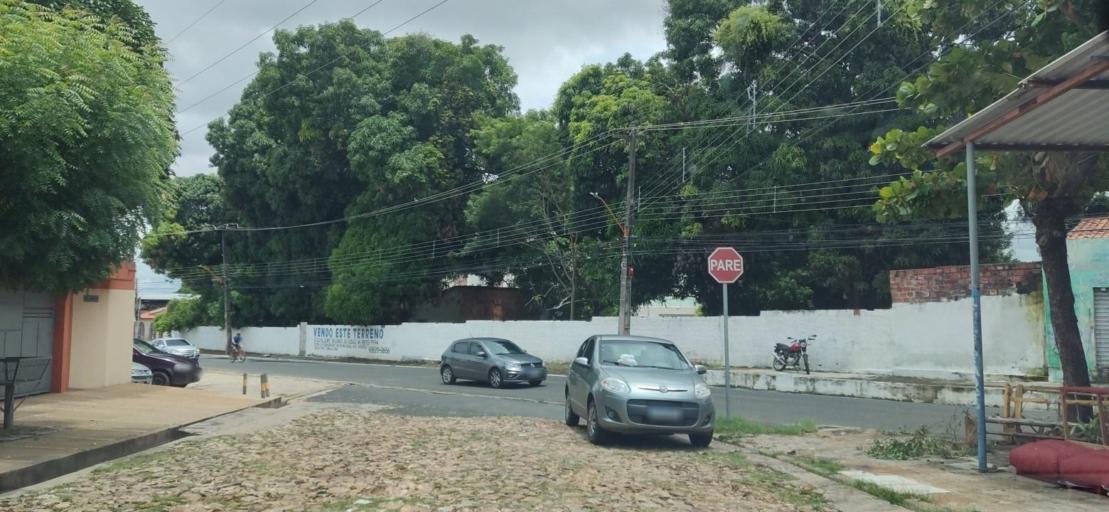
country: BR
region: Piaui
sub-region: Teresina
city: Teresina
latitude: -5.0755
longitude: -42.7654
